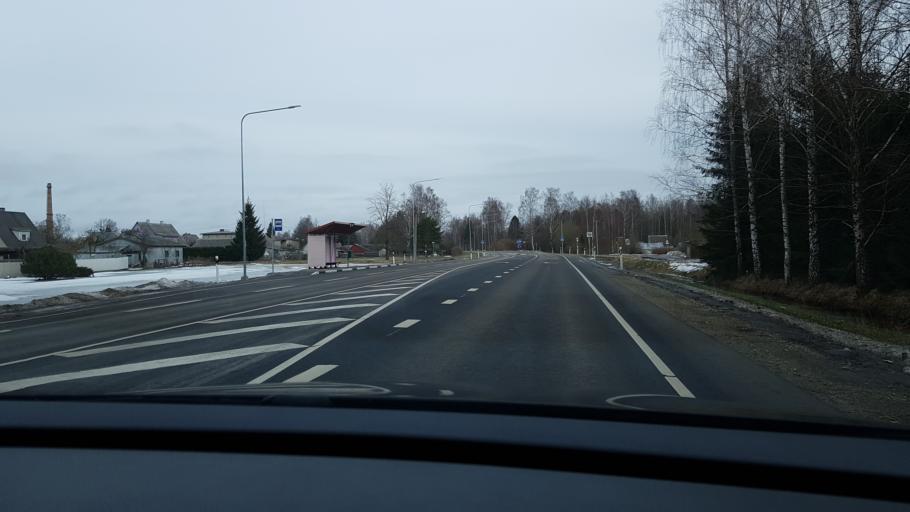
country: EE
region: Paernumaa
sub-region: Sindi linn
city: Sindi
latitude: 58.4057
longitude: 24.6642
